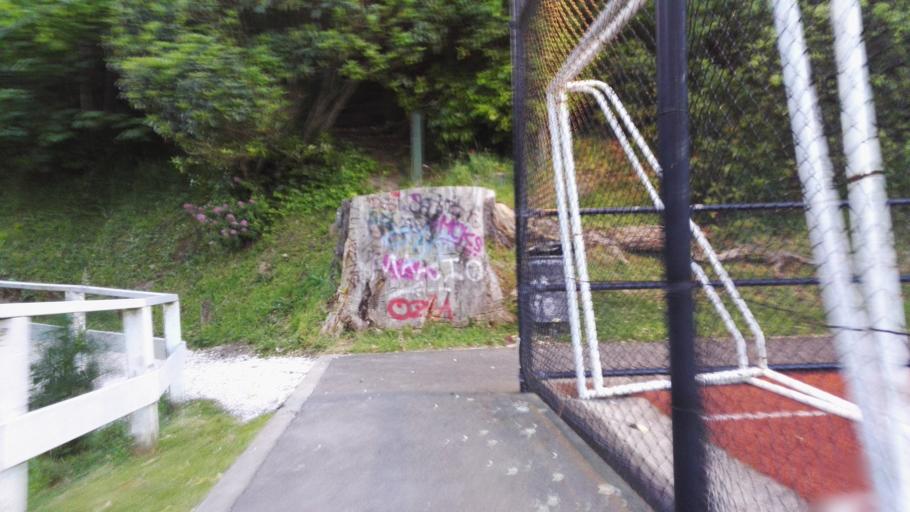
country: NZ
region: Wellington
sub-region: Wellington City
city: Kelburn
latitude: -41.2928
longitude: 174.7677
